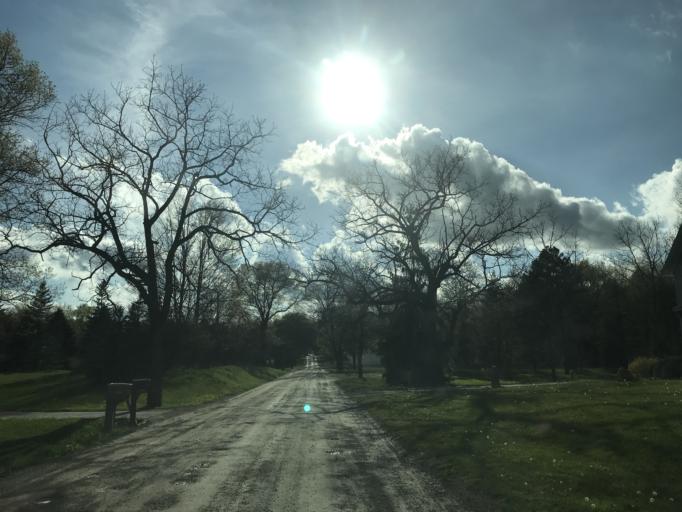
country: US
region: Michigan
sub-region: Livingston County
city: Brighton
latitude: 42.5462
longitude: -83.7194
